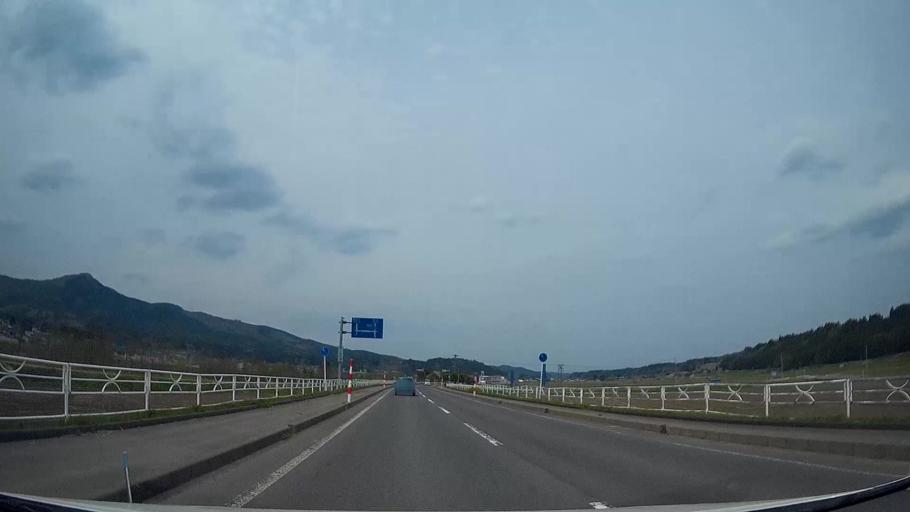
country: JP
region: Akita
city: Hanawa
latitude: 40.1415
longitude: 140.7981
